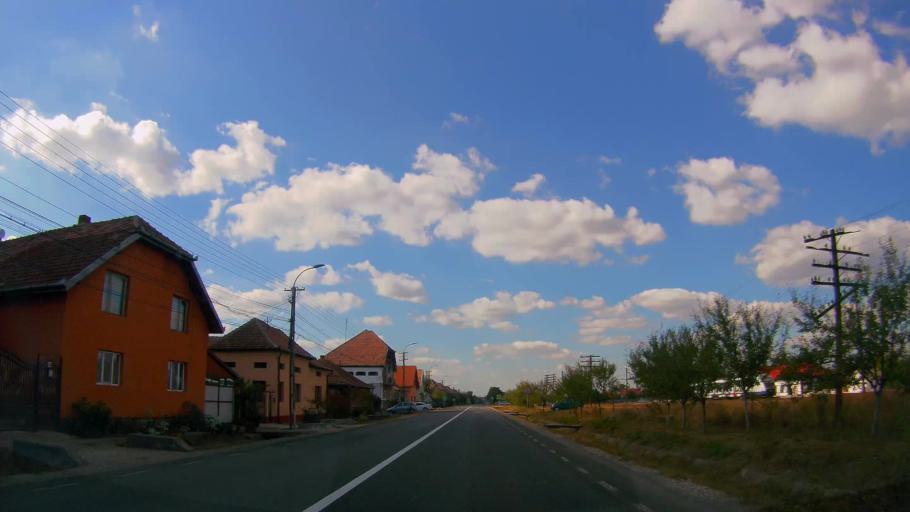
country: RO
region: Salaj
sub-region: Comuna Sarmasag
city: Sarmasag
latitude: 47.3417
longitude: 22.8300
